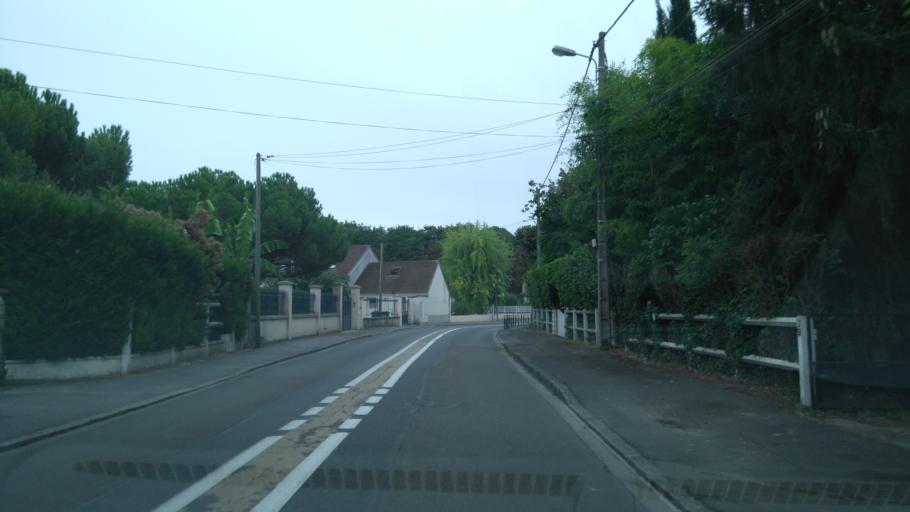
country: FR
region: Picardie
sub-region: Departement de l'Oise
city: Gouvieux
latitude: 49.1863
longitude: 2.4066
